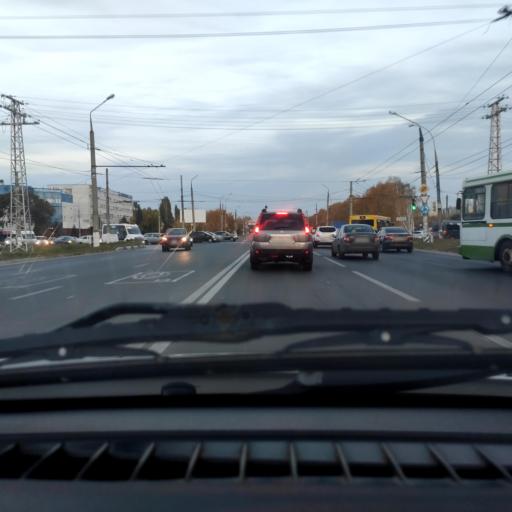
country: RU
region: Samara
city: Tol'yatti
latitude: 53.5522
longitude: 49.3013
